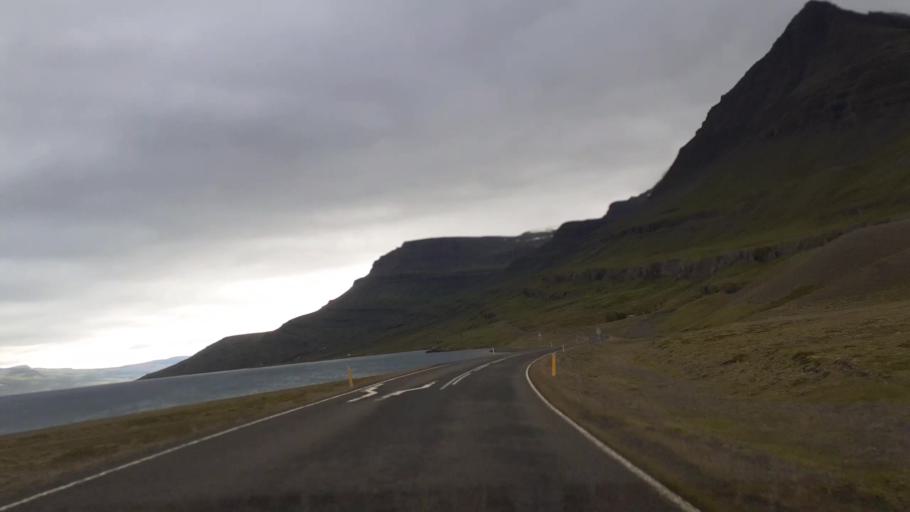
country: IS
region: East
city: Reydarfjoerdur
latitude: 65.0169
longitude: -14.2031
